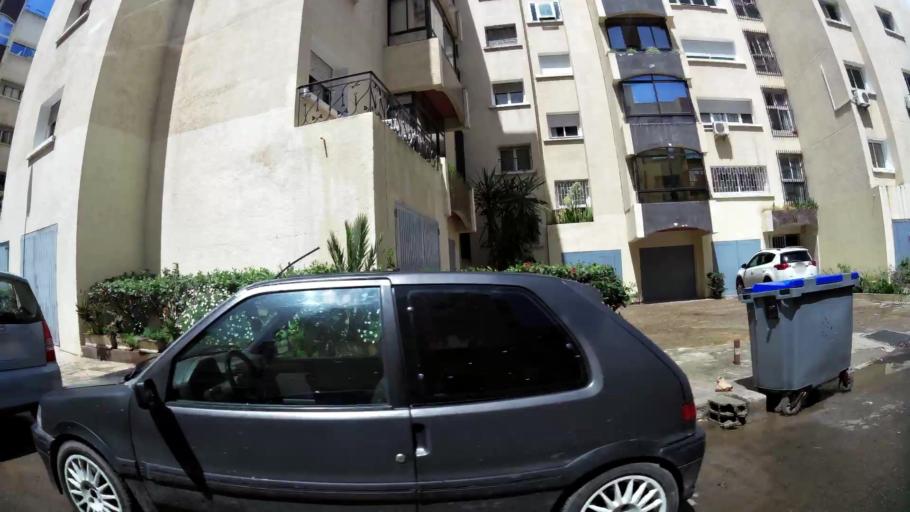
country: MA
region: Grand Casablanca
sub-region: Casablanca
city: Casablanca
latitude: 33.5713
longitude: -7.6419
